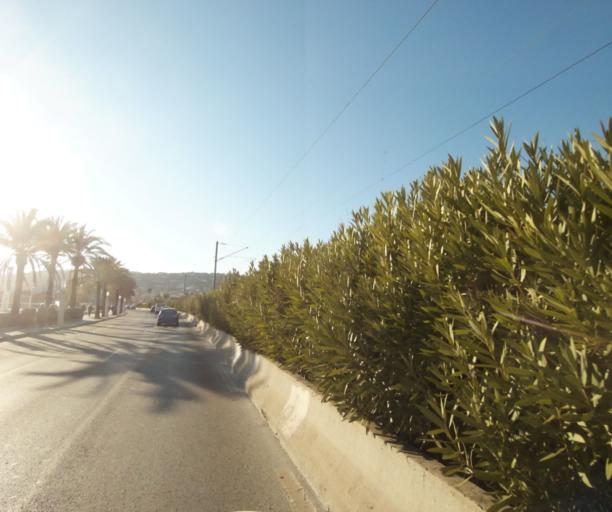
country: FR
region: Provence-Alpes-Cote d'Azur
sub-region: Departement des Alpes-Maritimes
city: Vallauris
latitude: 43.5702
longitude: 7.0863
